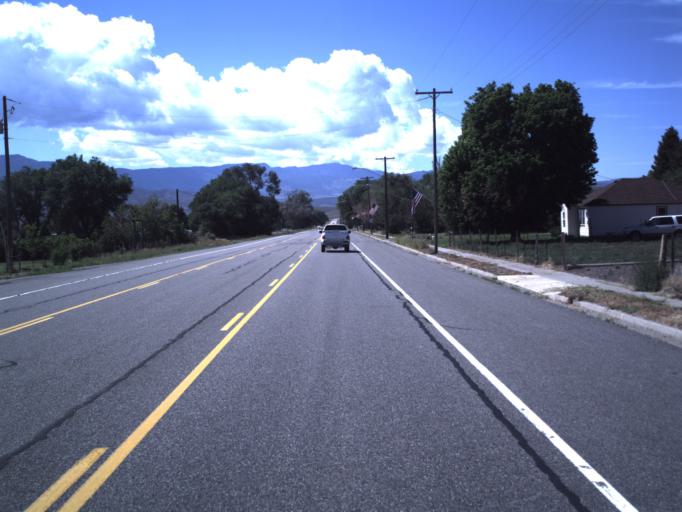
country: US
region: Utah
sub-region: Piute County
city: Junction
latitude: 38.2437
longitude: -112.2201
